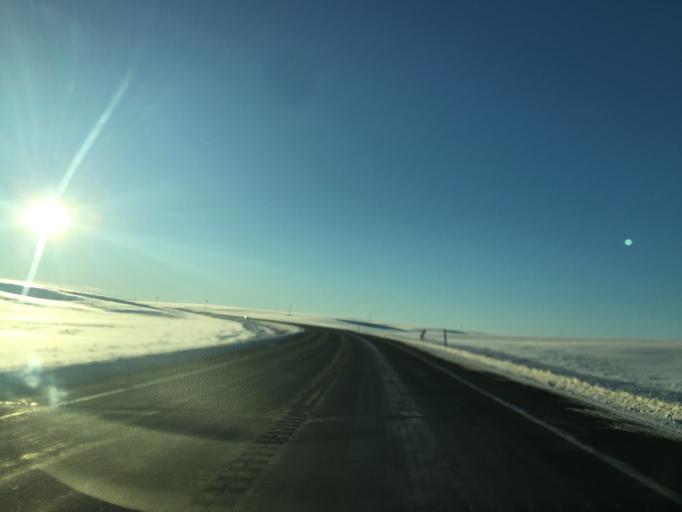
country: US
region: Washington
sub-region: Grant County
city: Soap Lake
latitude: 47.6066
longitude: -119.5049
